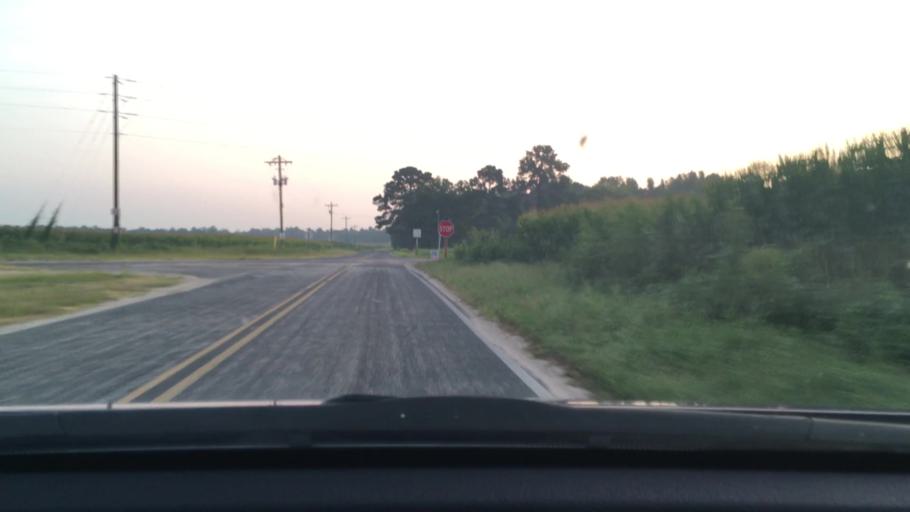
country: US
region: South Carolina
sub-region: Lee County
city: Bishopville
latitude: 34.1783
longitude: -80.1436
